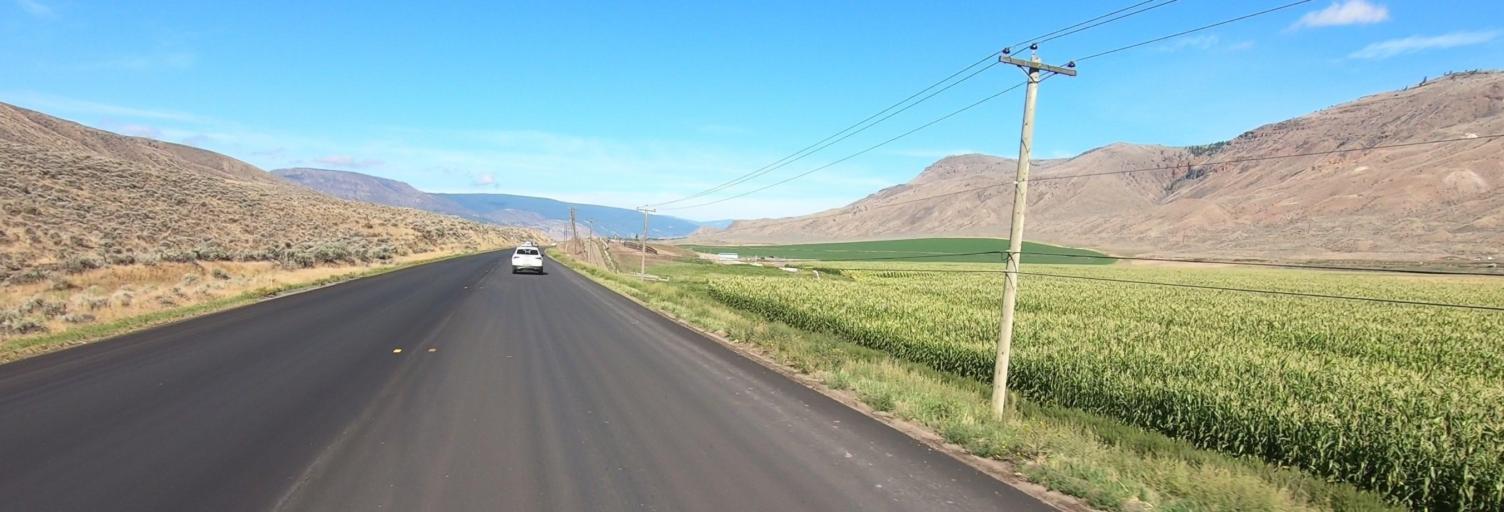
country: CA
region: British Columbia
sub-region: Thompson-Nicola Regional District
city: Ashcroft
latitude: 50.7880
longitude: -121.2261
